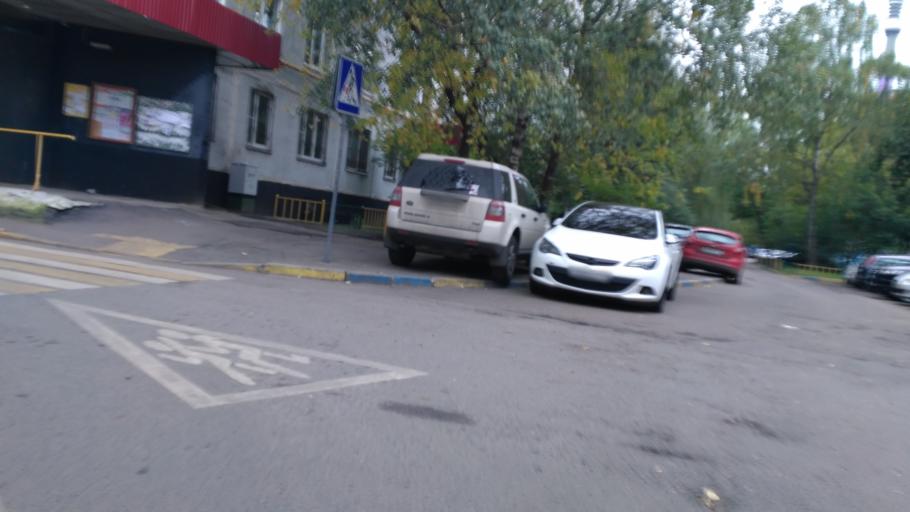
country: RU
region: Moscow
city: Ostankinskiy
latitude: 55.8186
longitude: 37.6269
